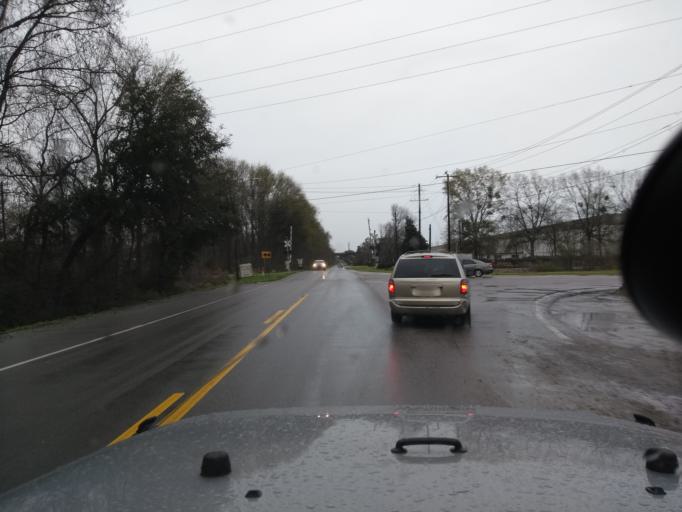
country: US
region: Georgia
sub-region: Chatham County
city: Savannah
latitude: 32.0851
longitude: -81.1348
